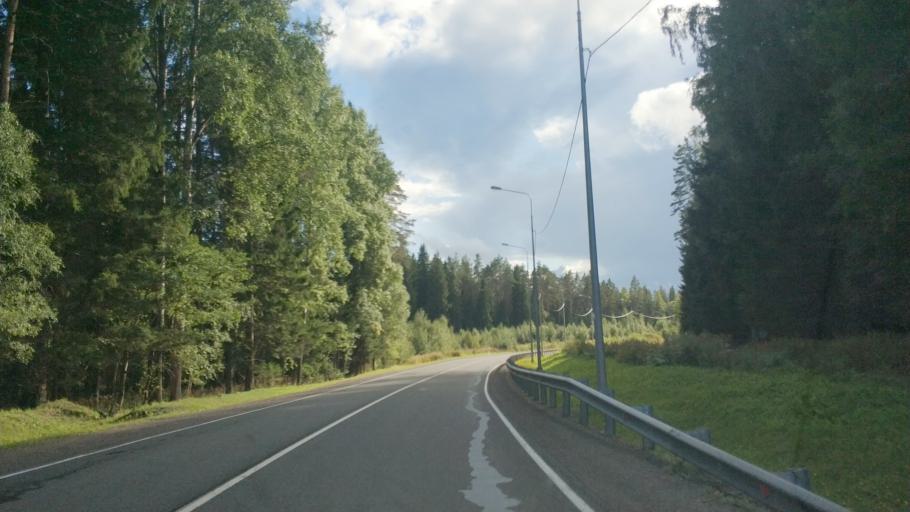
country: RU
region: Republic of Karelia
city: Lakhdenpokh'ya
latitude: 61.5116
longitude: 30.0973
